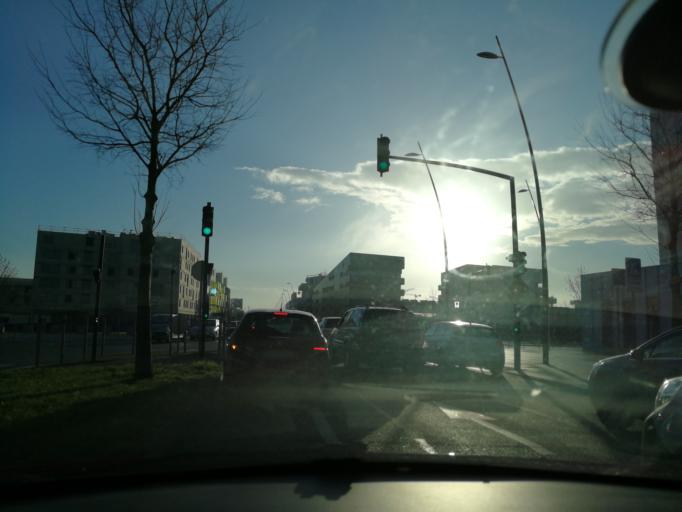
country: FR
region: Midi-Pyrenees
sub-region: Departement de la Haute-Garonne
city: Beauzelle
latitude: 43.6554
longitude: 1.3671
